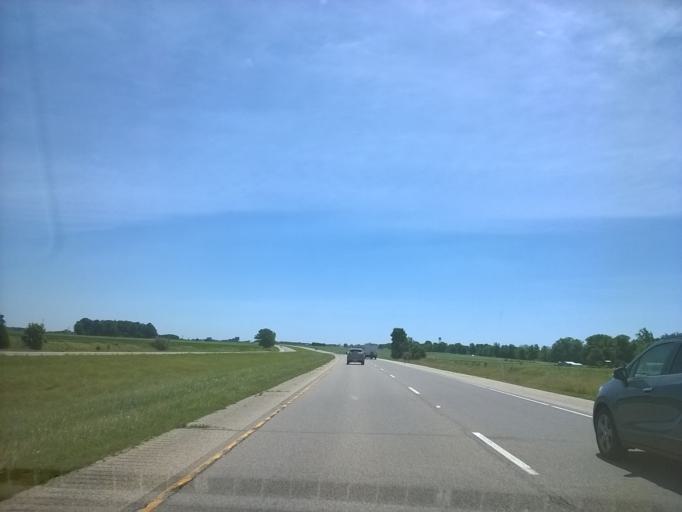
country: US
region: Indiana
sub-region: Decatur County
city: Greensburg
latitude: 39.3179
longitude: -85.3655
